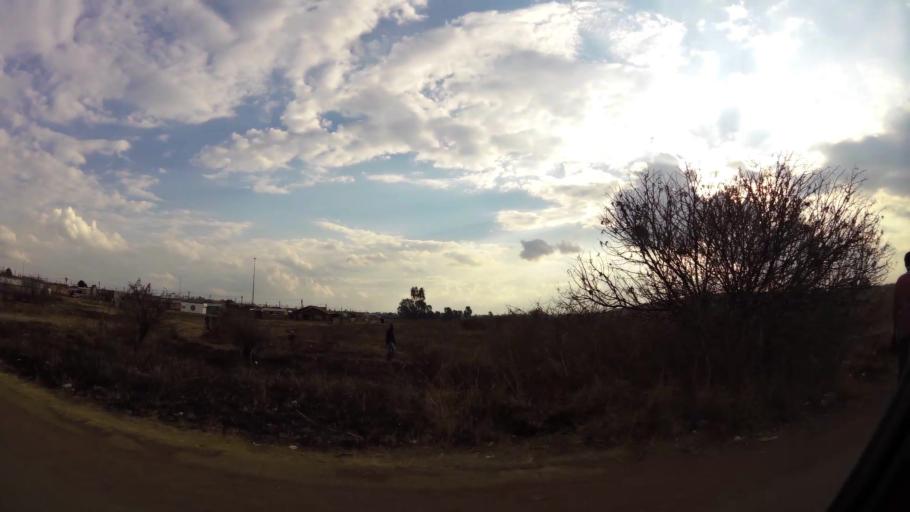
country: ZA
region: Gauteng
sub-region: Sedibeng District Municipality
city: Vanderbijlpark
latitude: -26.6731
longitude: 27.8683
